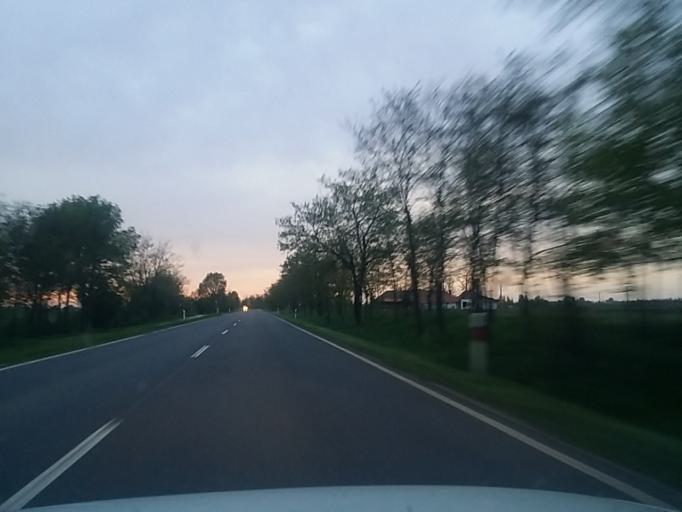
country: HU
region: Bekes
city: Csorvas
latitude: 46.7238
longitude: 20.9241
